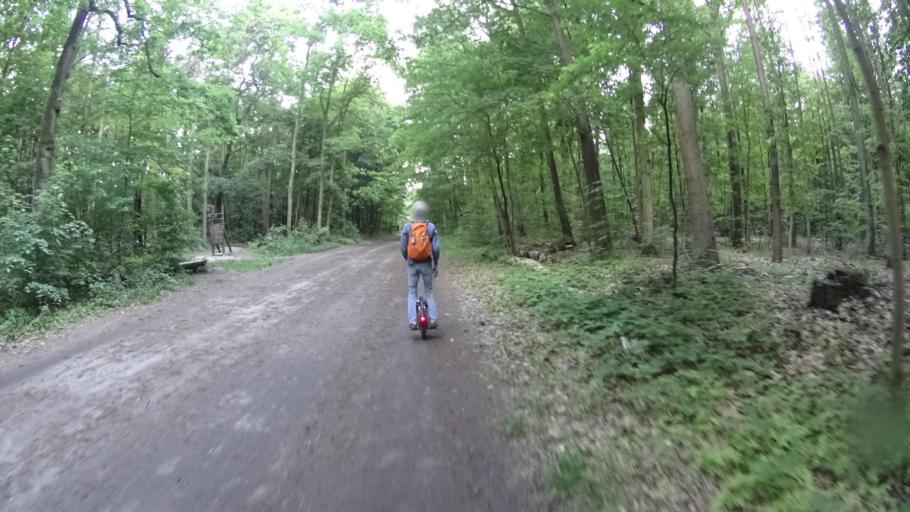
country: PL
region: Masovian Voivodeship
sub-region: Warszawa
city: Kabaty
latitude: 52.1196
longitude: 21.0855
